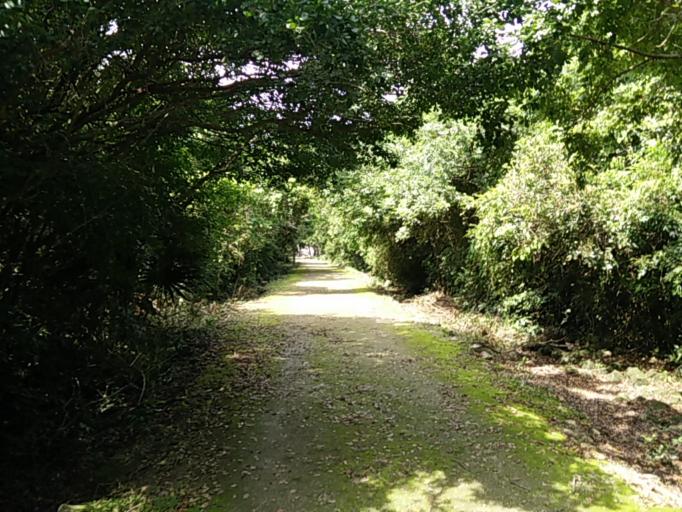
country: MX
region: Quintana Roo
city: San Miguel de Cozumel
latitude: 20.5016
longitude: -86.8503
